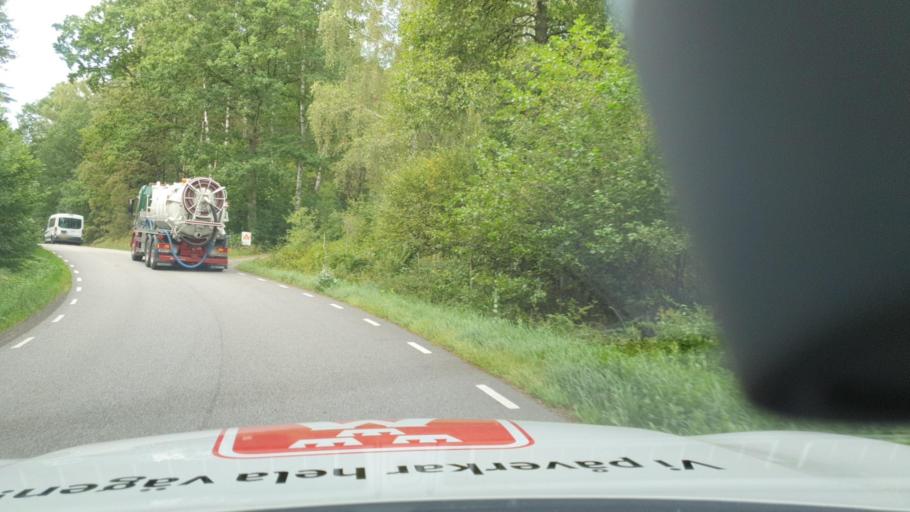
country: SE
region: Vaestra Goetaland
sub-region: Marks Kommun
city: Kinna
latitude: 57.4275
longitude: 12.6795
